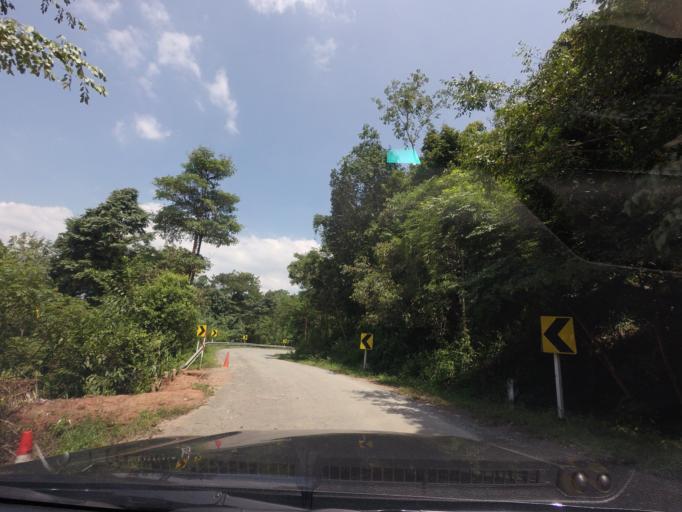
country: TH
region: Loei
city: Na Haeo
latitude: 17.6094
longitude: 100.8943
